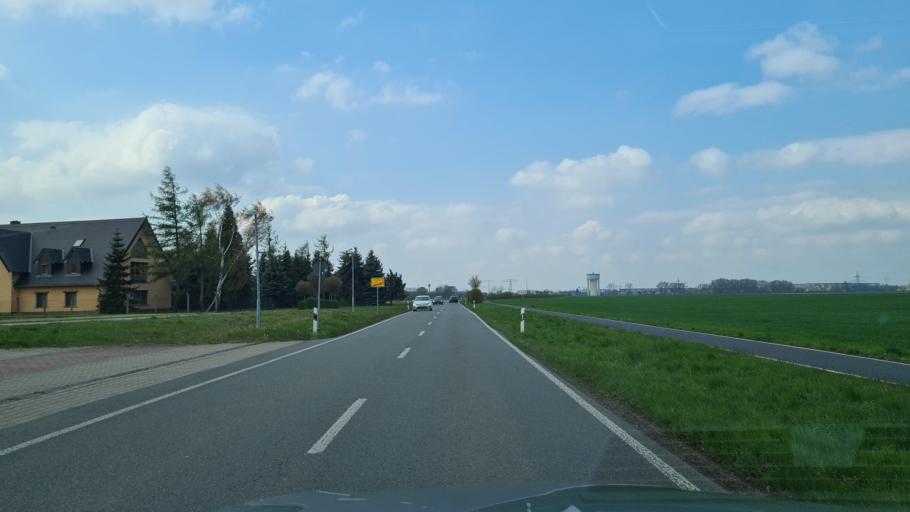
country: DE
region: Saxony
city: Nauwalde
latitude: 51.3939
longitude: 13.4617
